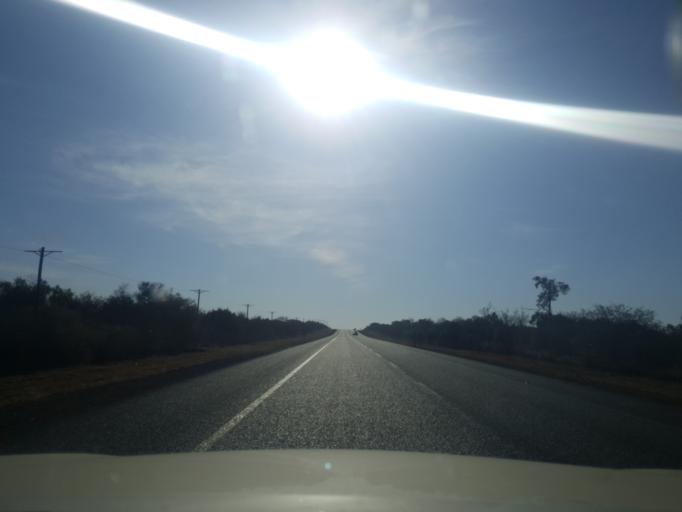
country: ZA
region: North-West
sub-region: Ngaka Modiri Molema District Municipality
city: Zeerust
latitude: -25.5240
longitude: 26.0106
